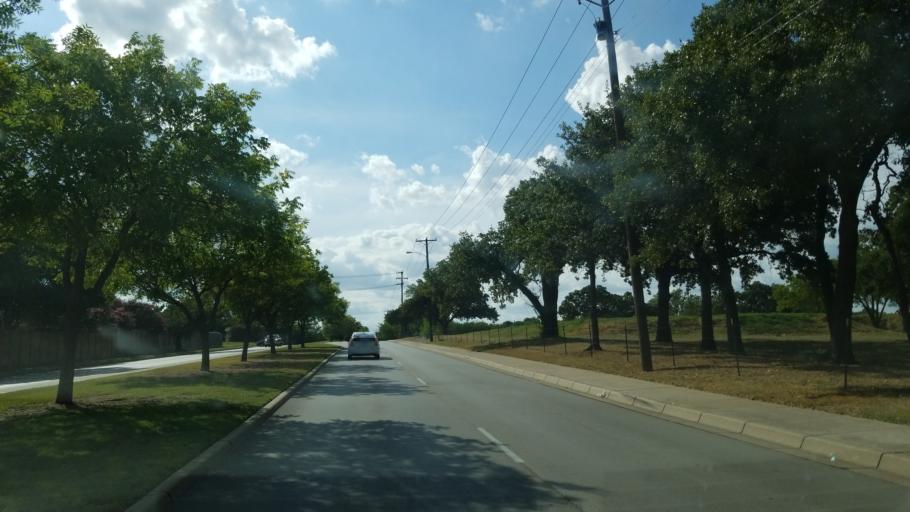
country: US
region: Texas
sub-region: Tarrant County
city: Bedford
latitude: 32.8521
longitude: -97.1356
